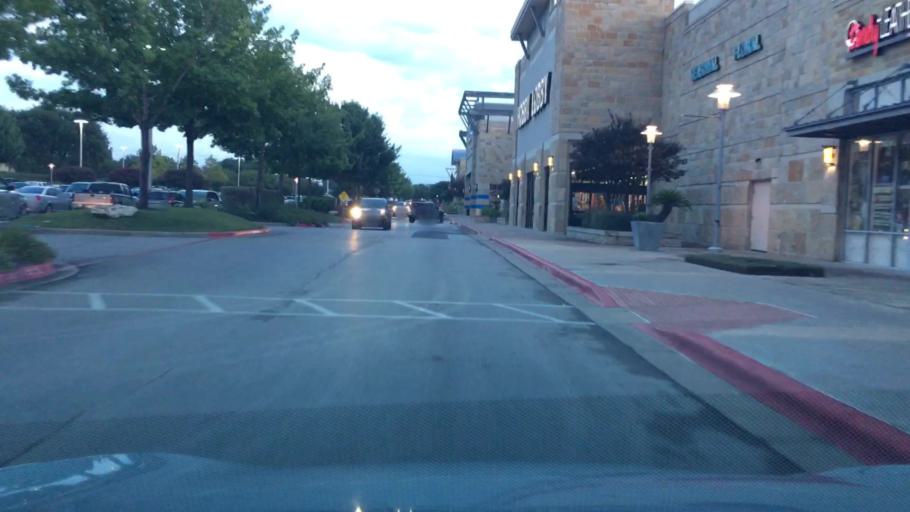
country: US
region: Texas
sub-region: Travis County
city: Onion Creek
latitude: 30.1606
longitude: -97.7943
